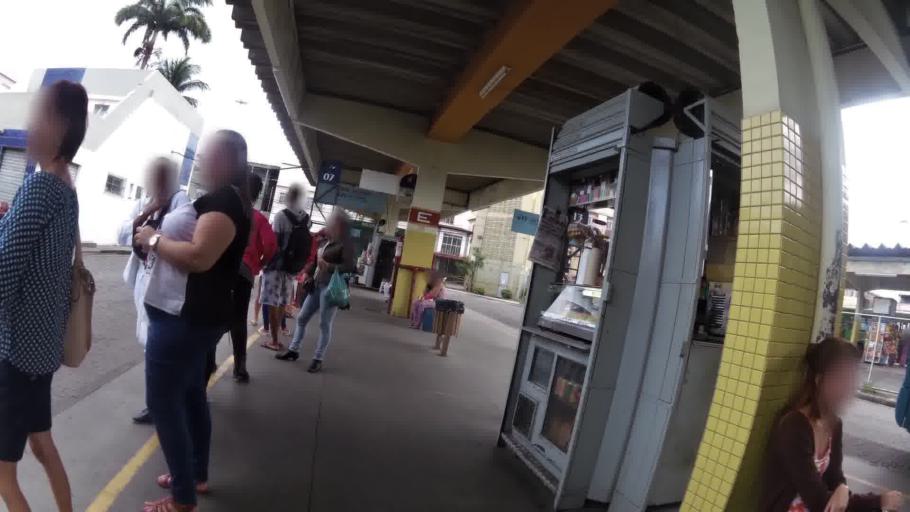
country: BR
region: Espirito Santo
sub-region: Vila Velha
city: Vila Velha
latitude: -20.3465
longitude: -40.3155
